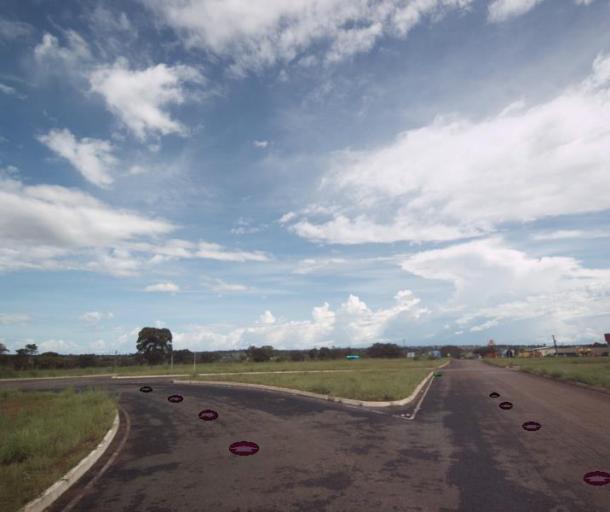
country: BR
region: Goias
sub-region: Sao Miguel Do Araguaia
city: Sao Miguel do Araguaia
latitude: -13.2848
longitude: -50.1838
